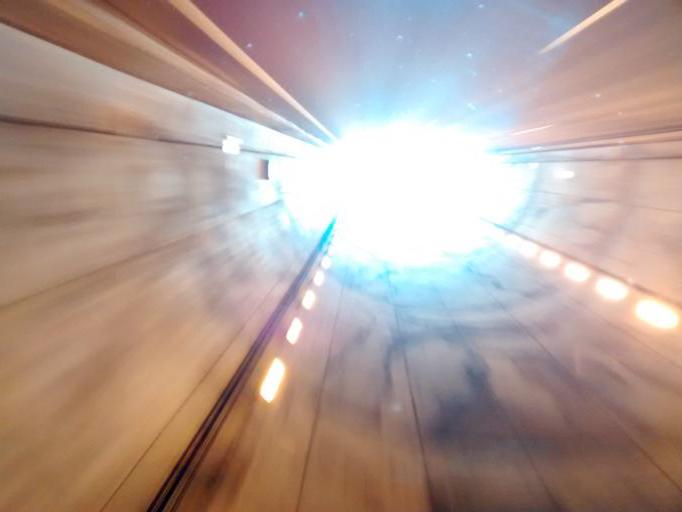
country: ES
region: Cantabria
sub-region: Provincia de Cantabria
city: Cartes
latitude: 43.3062
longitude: -4.0791
